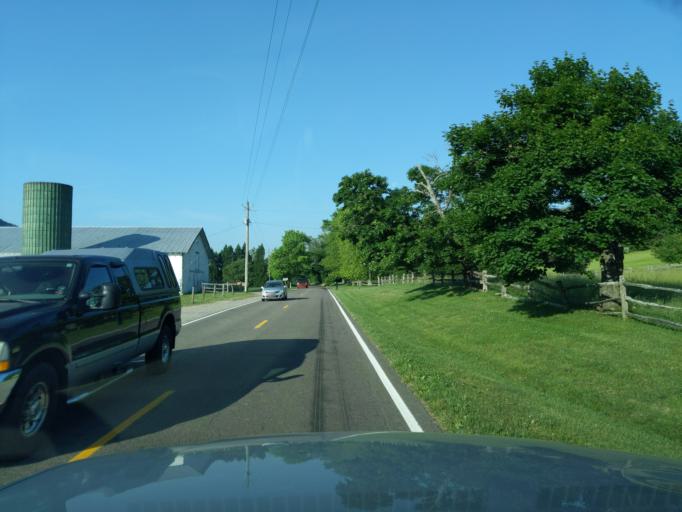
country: US
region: North Carolina
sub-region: Henderson County
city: Hoopers Creek
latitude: 35.4675
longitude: -82.4609
